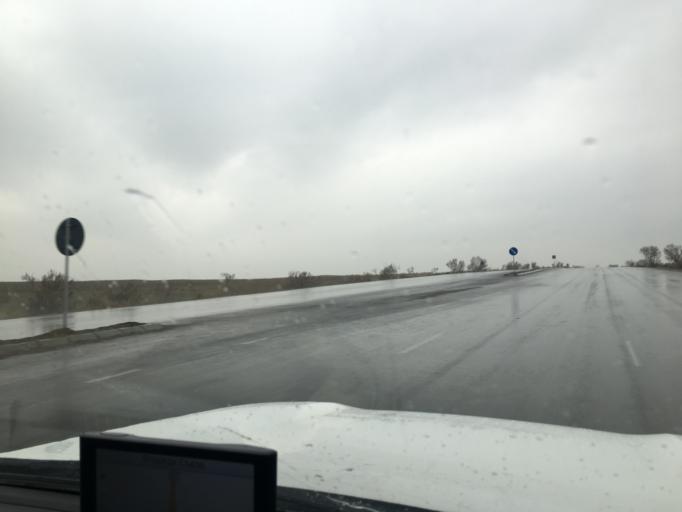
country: TM
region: Ahal
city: Annau
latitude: 37.8558
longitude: 58.6889
